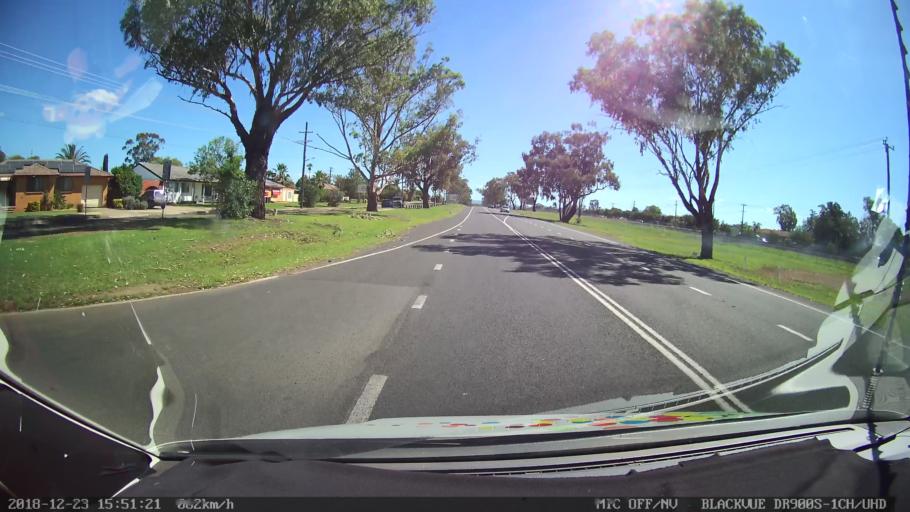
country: AU
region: New South Wales
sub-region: Tamworth Municipality
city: South Tamworth
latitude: -31.1120
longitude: 150.8965
